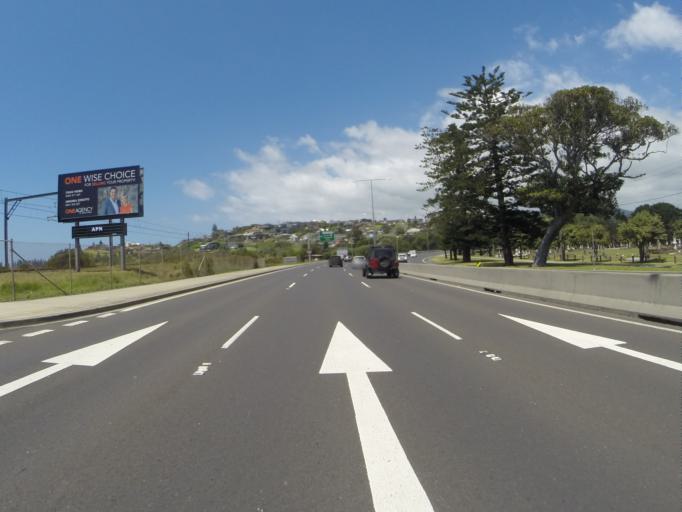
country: AU
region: New South Wales
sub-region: Kiama
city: Kiama
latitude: -34.6594
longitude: 150.8536
